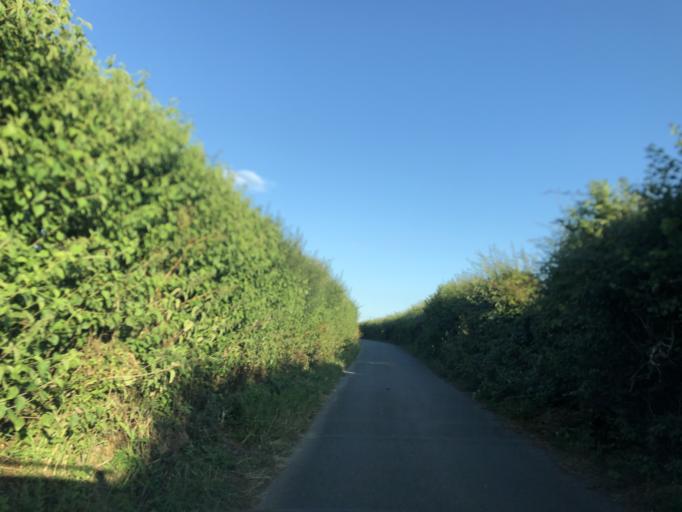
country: GB
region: England
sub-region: Isle of Wight
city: Shalfleet
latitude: 50.6384
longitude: -1.3994
